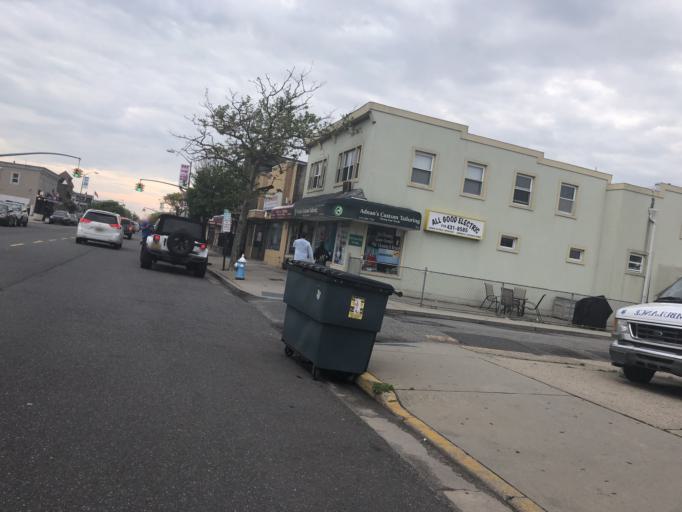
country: US
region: New York
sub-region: Nassau County
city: Harbor Isle
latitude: 40.5861
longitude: -73.6929
